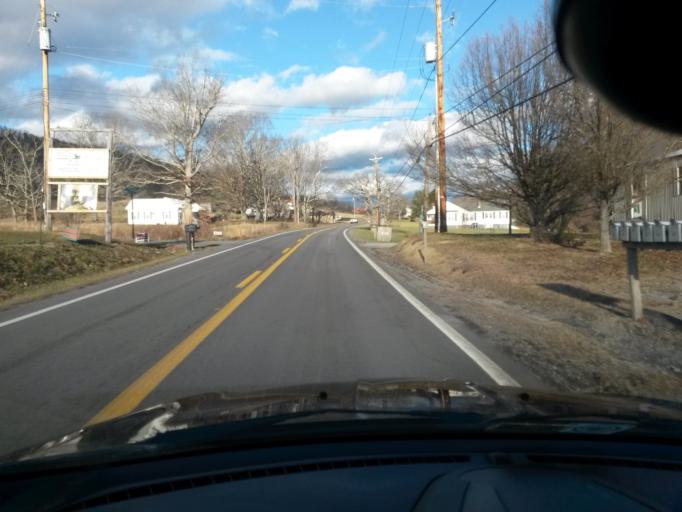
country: US
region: Virginia
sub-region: Giles County
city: Pearisburg
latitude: 37.4093
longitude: -80.7554
